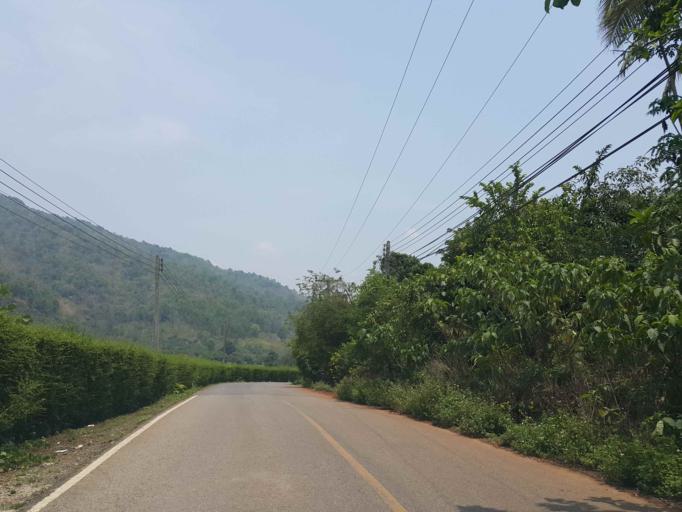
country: TH
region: Chiang Mai
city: Mae Taeng
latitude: 19.1801
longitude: 98.8562
